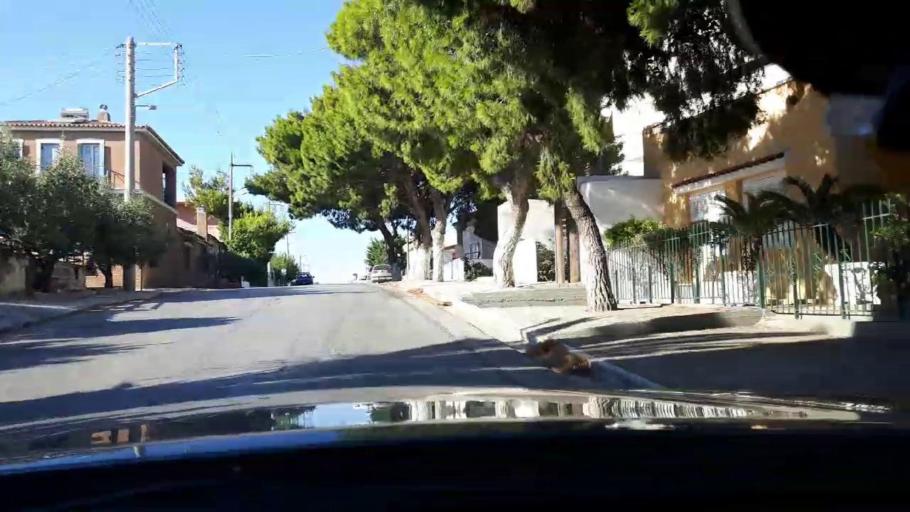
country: GR
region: Attica
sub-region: Nomarchia Anatolikis Attikis
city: Markopoulo
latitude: 37.8821
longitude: 23.9360
